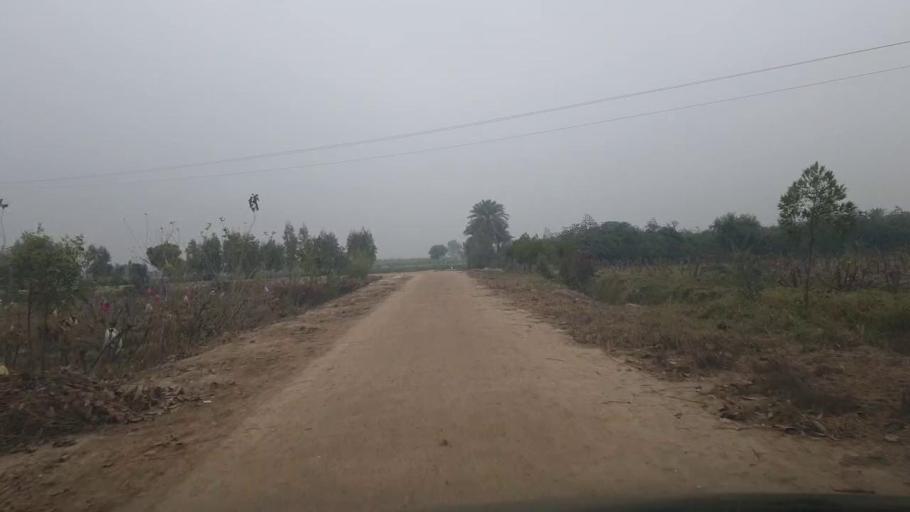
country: PK
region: Sindh
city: Tando Adam
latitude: 25.7687
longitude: 68.6403
